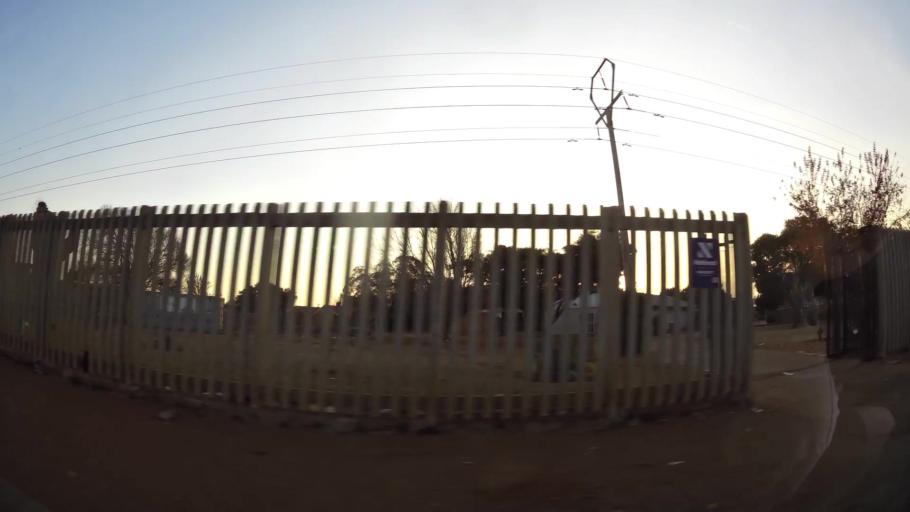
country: ZA
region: Gauteng
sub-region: West Rand District Municipality
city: Randfontein
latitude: -26.2012
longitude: 27.7081
